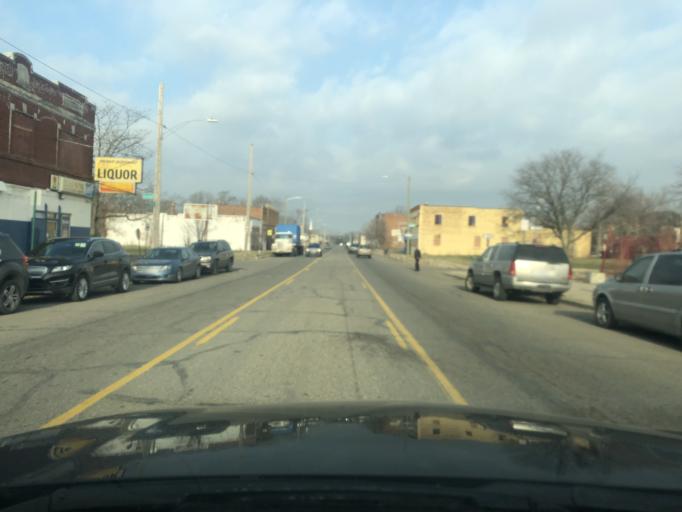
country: US
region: Michigan
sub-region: Wayne County
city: Highland Park
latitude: 42.3942
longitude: -83.1228
